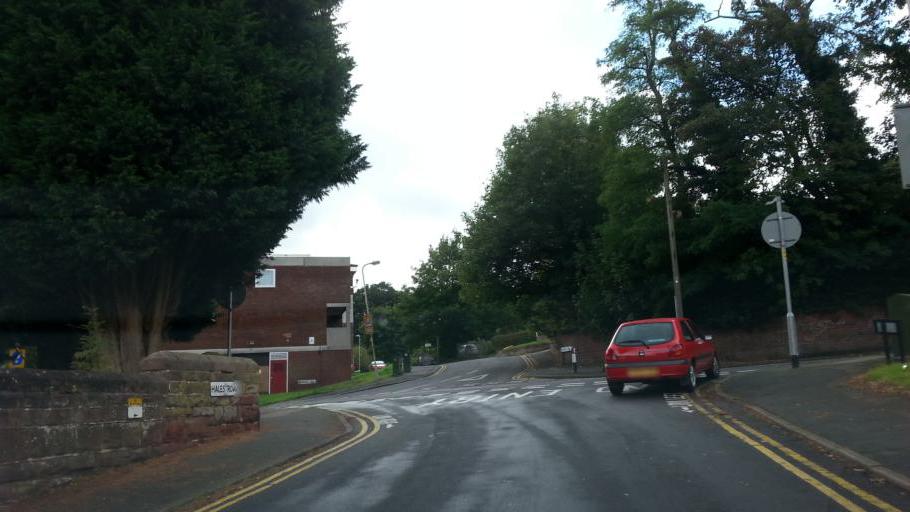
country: GB
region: England
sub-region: Dudley
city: Halesowen
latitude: 52.4503
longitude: -2.0548
